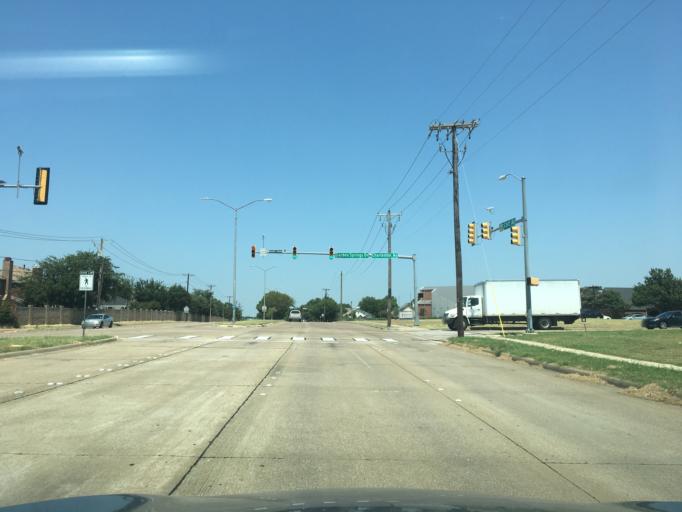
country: US
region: Texas
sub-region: Tarrant County
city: Crowley
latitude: 32.6182
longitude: -97.3703
